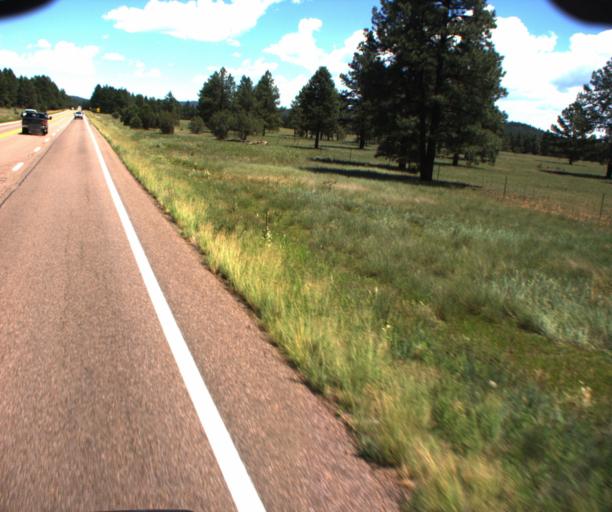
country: US
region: Arizona
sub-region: Navajo County
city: Lake of the Woods
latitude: 34.1152
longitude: -110.1382
